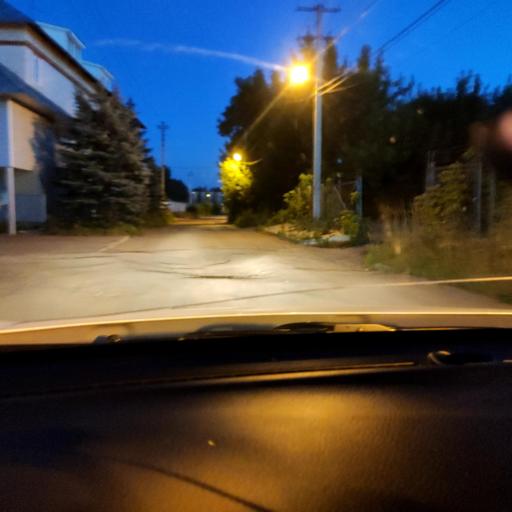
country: RU
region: Tatarstan
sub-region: Gorod Kazan'
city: Kazan
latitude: 55.8666
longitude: 49.1068
